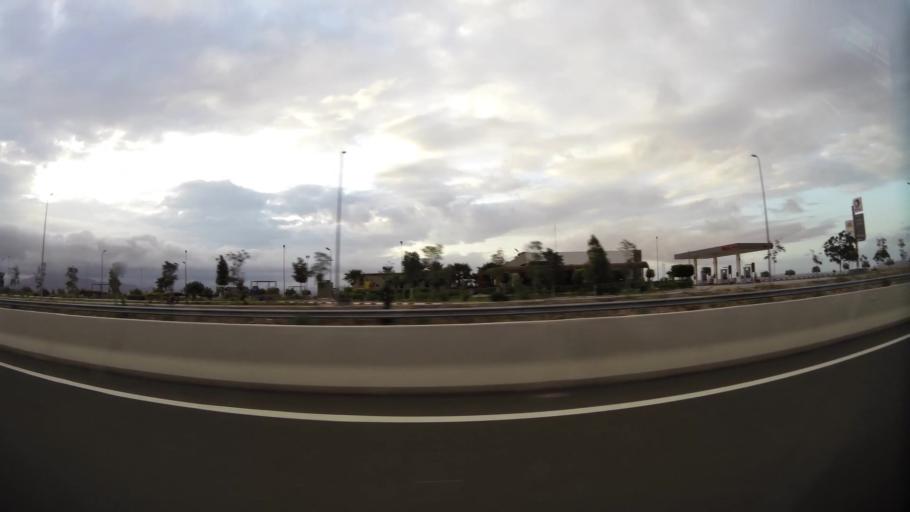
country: MA
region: Taza-Al Hoceima-Taounate
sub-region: Taza
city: Guercif
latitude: 34.4106
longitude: -3.1643
